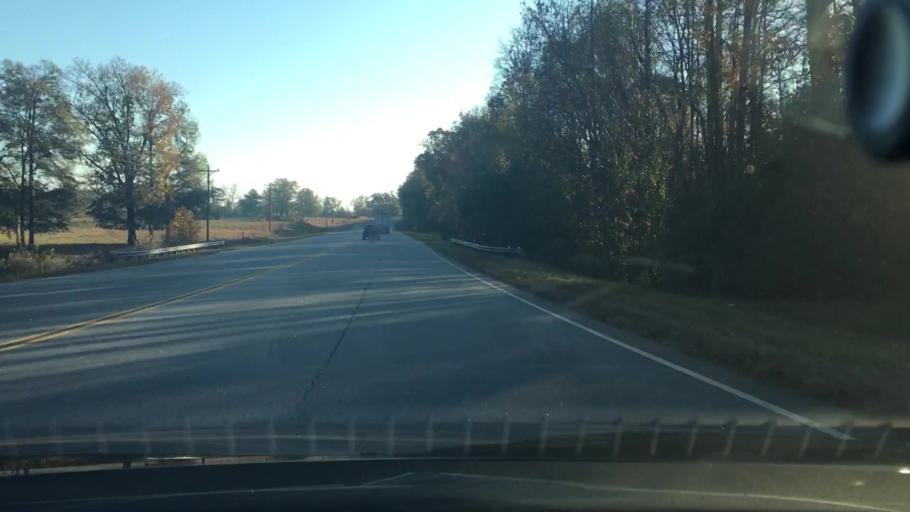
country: US
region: Georgia
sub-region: Coweta County
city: Senoia
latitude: 33.2485
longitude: -84.4491
